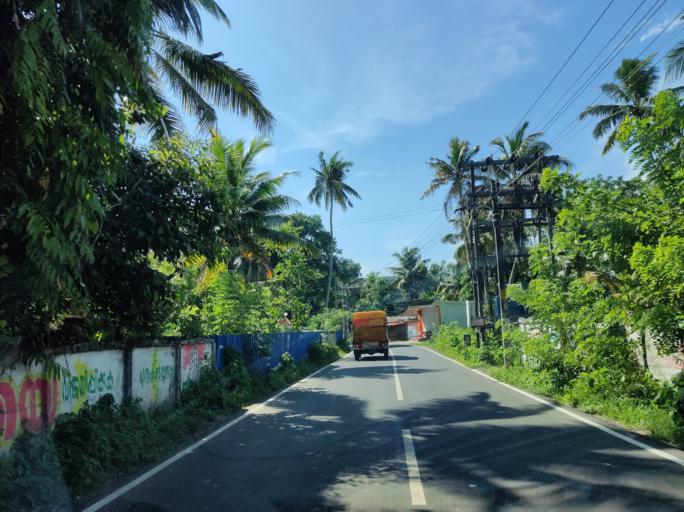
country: IN
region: Kerala
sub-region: Alappuzha
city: Kayankulam
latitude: 9.2802
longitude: 76.3993
